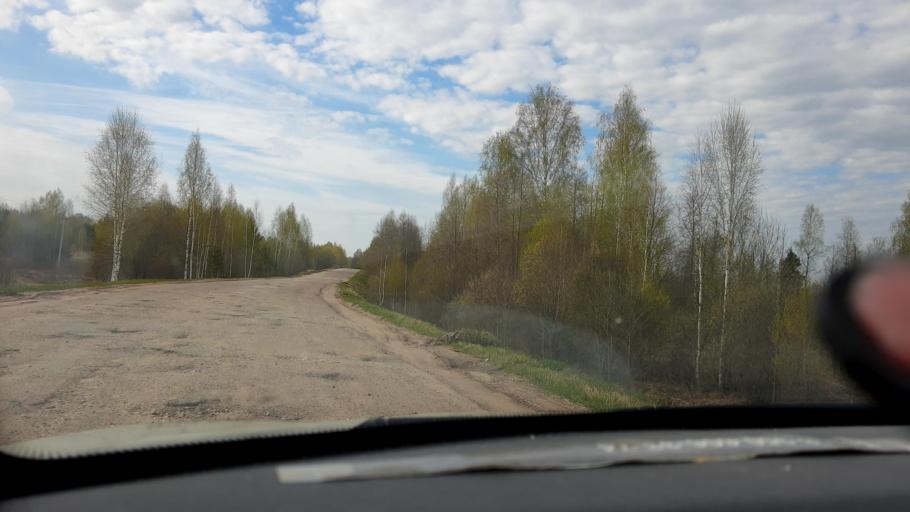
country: RU
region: Mariy-El
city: Kilemary
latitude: 56.8321
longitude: 46.8315
